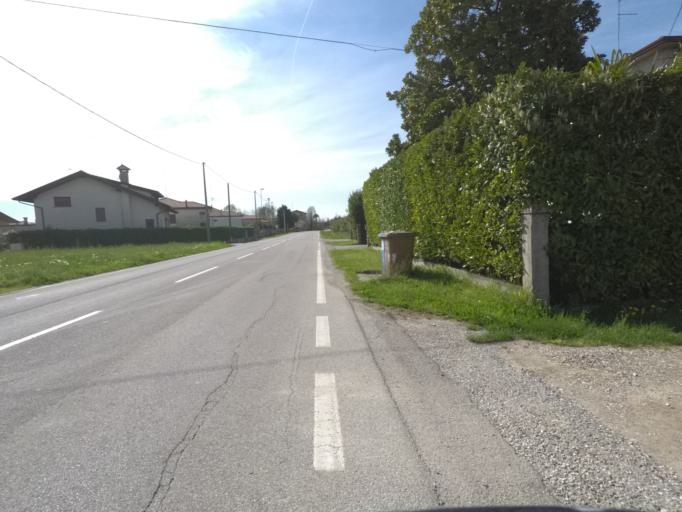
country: IT
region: Friuli Venezia Giulia
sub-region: Provincia di Pordenone
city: Fiume Veneto
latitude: 45.9338
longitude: 12.7198
